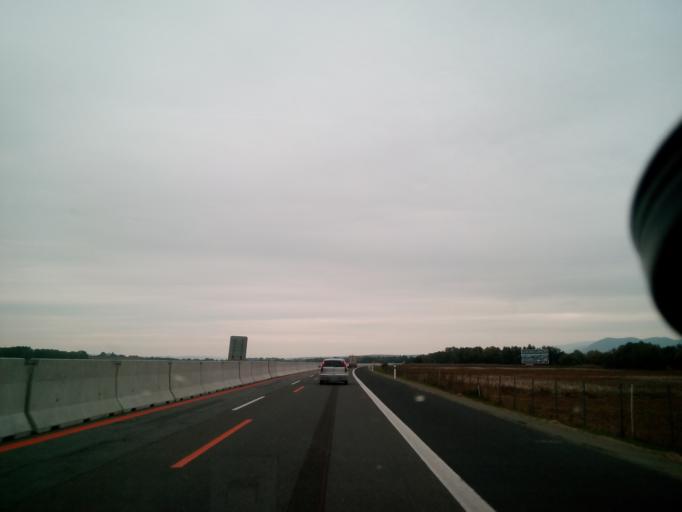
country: SK
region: Kosicky
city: Kosice
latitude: 48.8042
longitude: 21.3097
